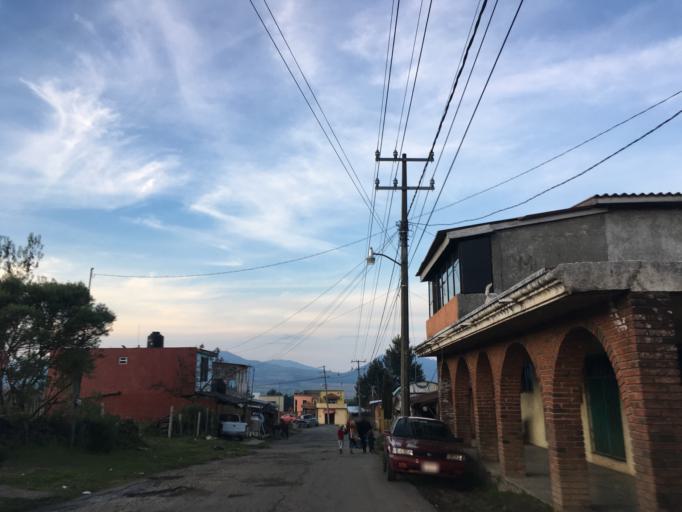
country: MX
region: Michoacan
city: Charapan
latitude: 19.6118
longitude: -102.2330
